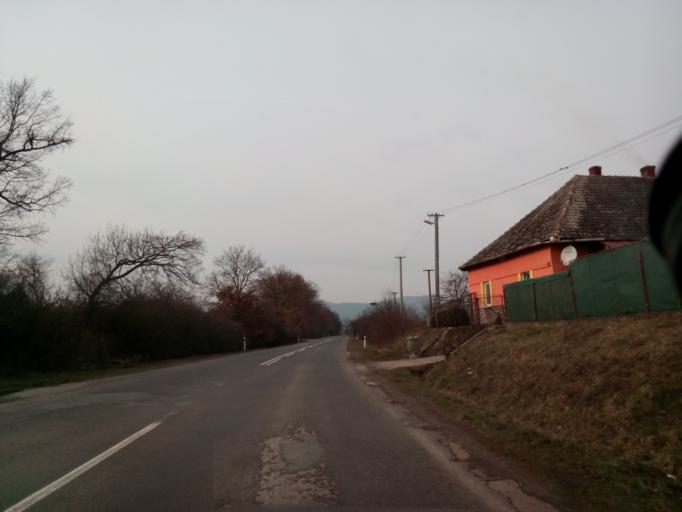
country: SK
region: Kosicky
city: Secovce
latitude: 48.6232
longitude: 21.5893
